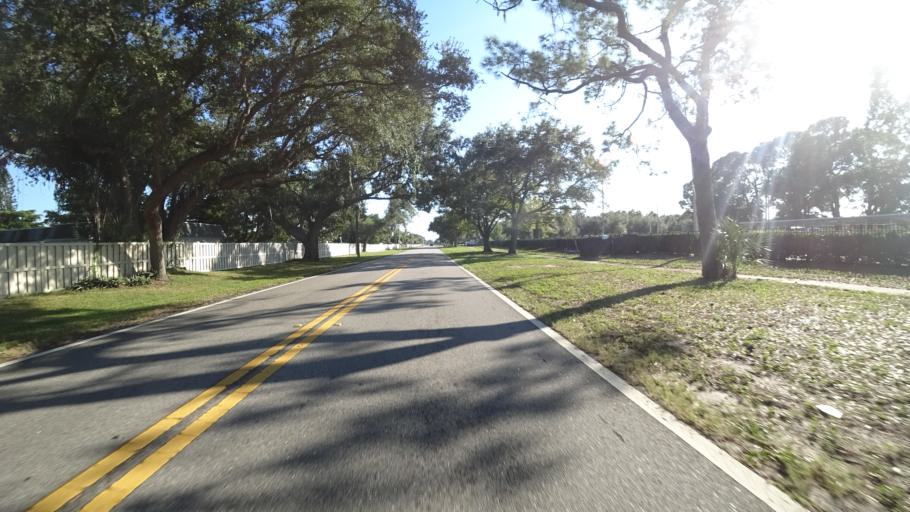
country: US
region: Florida
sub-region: Manatee County
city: South Bradenton
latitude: 27.4715
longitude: -82.6041
